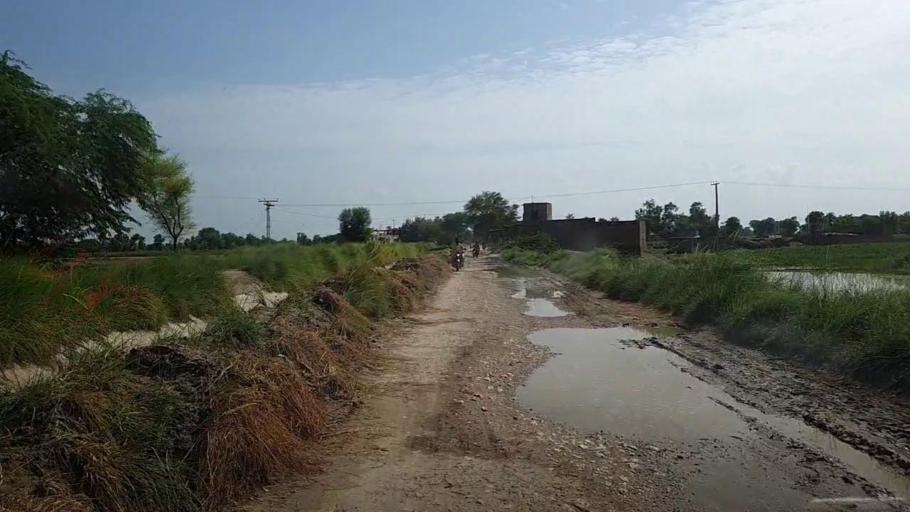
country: PK
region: Sindh
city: Bhiria
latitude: 26.8796
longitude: 68.2312
